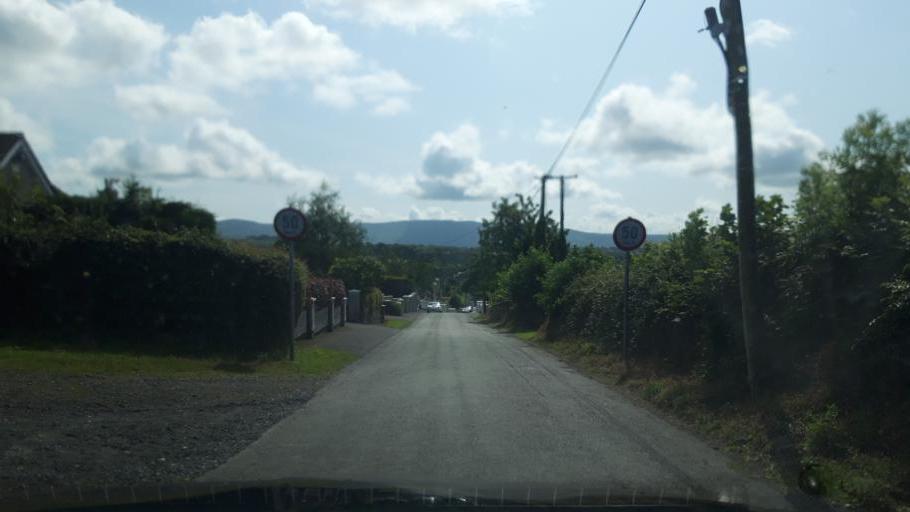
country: IE
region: Leinster
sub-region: Kilkenny
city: Graiguenamanagh
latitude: 52.5466
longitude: -6.9655
